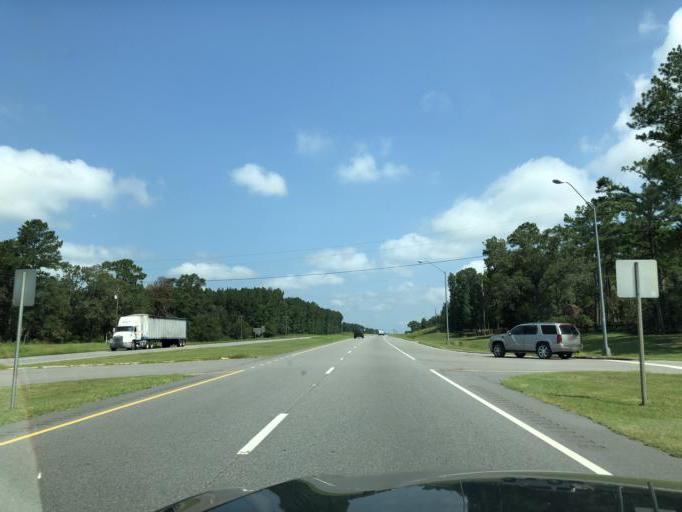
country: US
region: Alabama
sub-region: Houston County
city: Cottonwood
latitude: 31.0095
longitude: -85.4078
